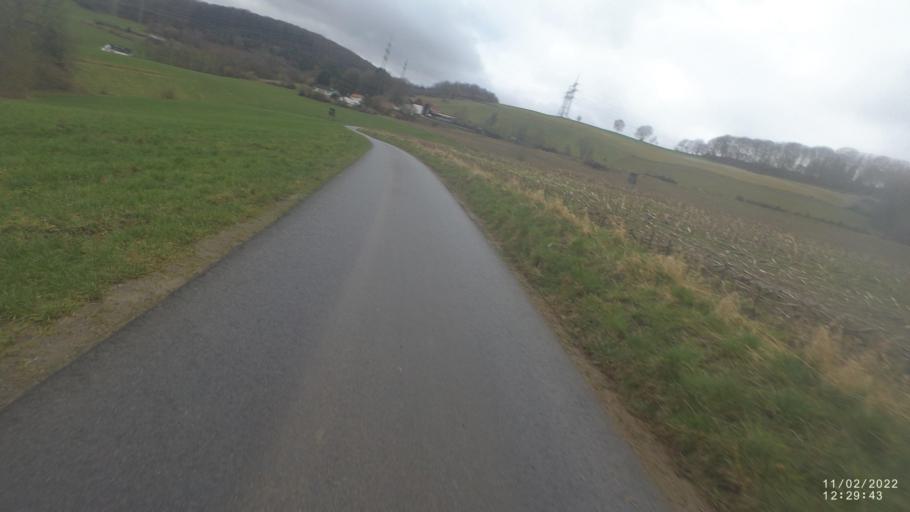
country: DE
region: North Rhine-Westphalia
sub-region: Regierungsbezirk Arnsberg
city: Nachrodt-Wiblingwerde
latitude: 51.3160
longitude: 7.6312
